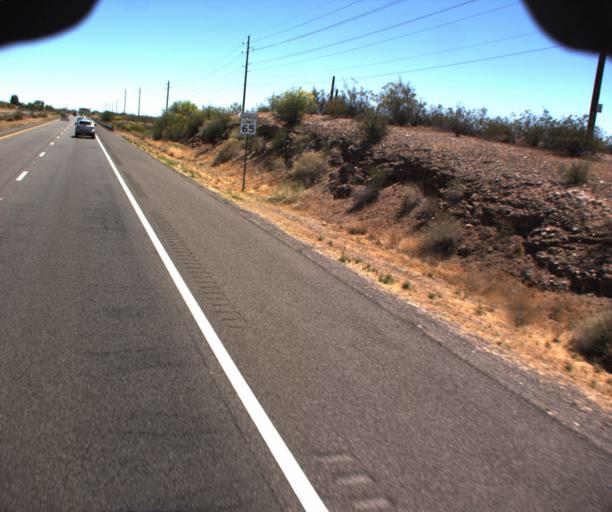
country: US
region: Arizona
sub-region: Maricopa County
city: Wickenburg
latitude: 33.8620
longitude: -112.6315
